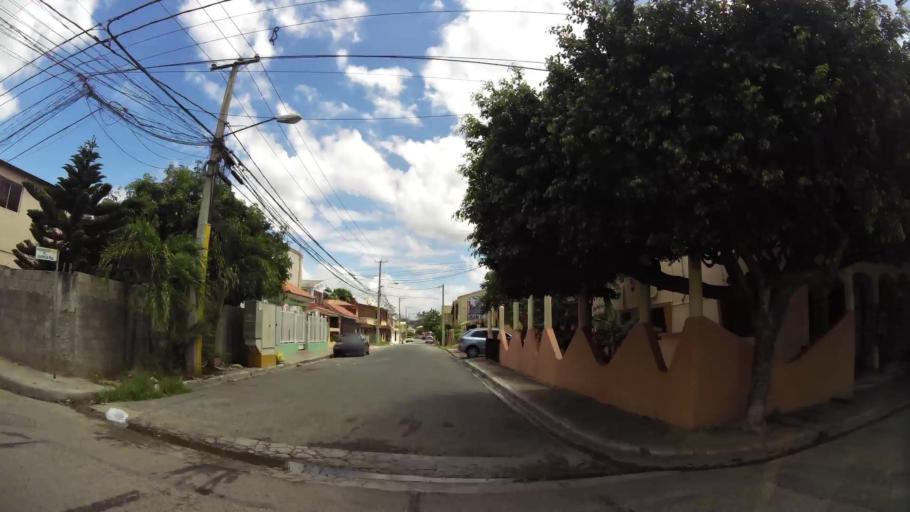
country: DO
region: San Cristobal
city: San Cristobal
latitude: 18.4130
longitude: -70.1031
